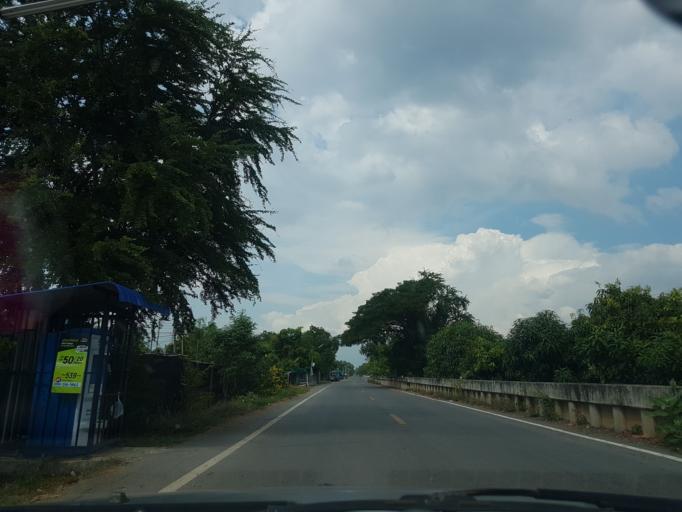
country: TH
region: Sara Buri
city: Nong Khae
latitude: 14.2497
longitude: 100.8913
